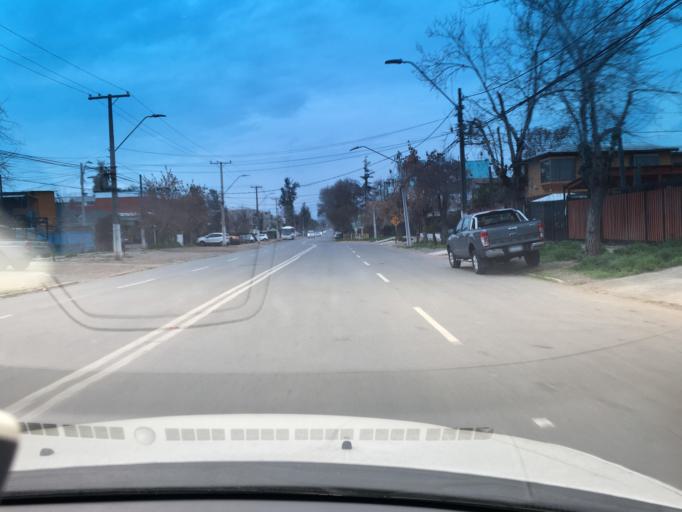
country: CL
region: Santiago Metropolitan
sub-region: Provincia de Santiago
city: Villa Presidente Frei, Nunoa, Santiago, Chile
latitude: -33.4885
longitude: -70.6062
